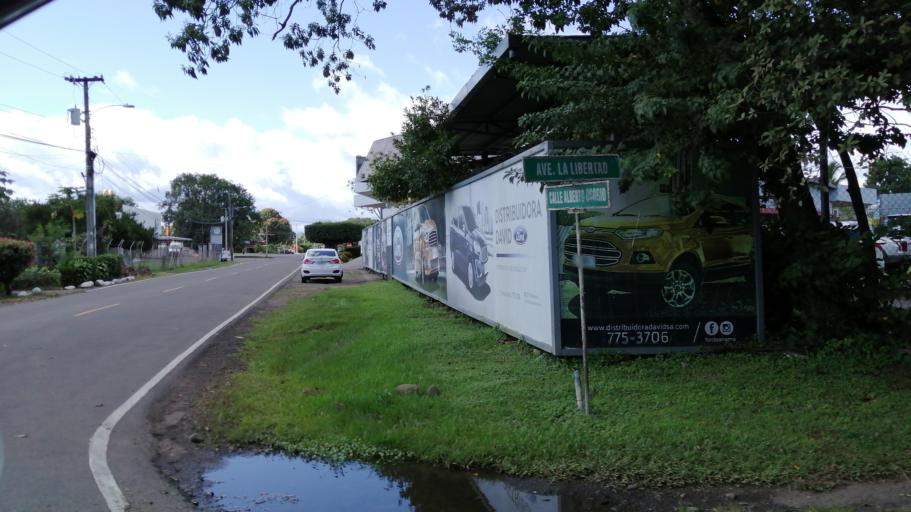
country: PA
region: Chiriqui
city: David
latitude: 8.4457
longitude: -82.4256
